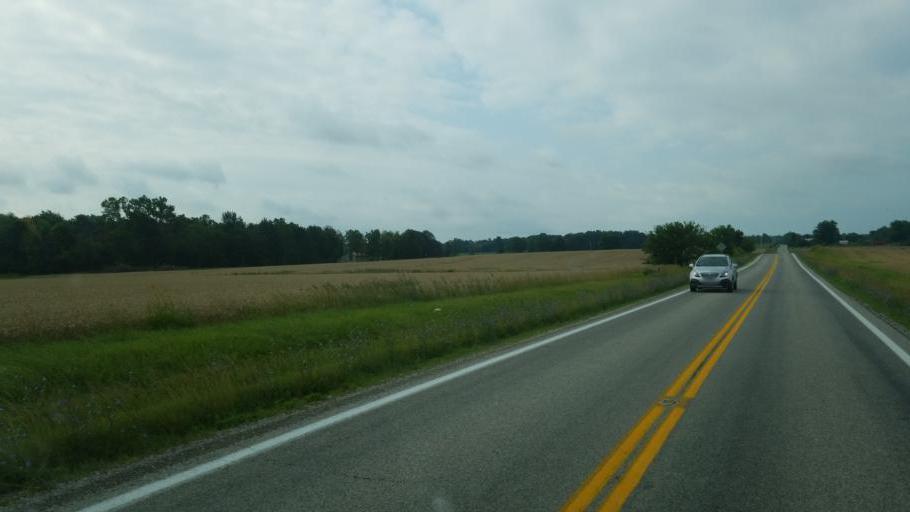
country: US
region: Ohio
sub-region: Knox County
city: Centerburg
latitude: 40.3890
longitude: -82.6962
